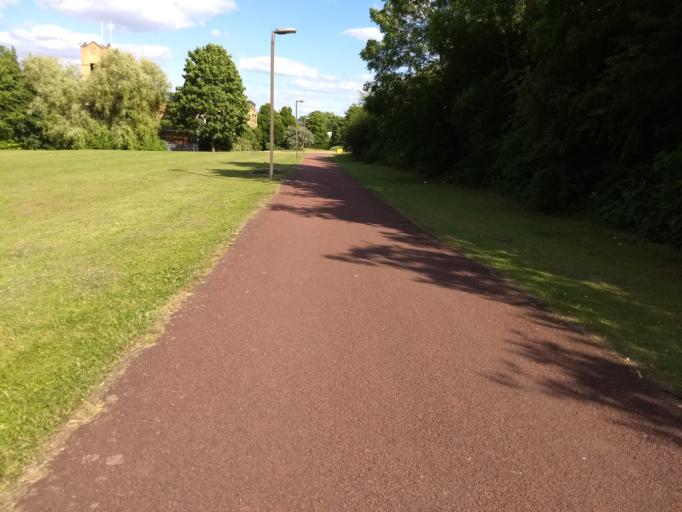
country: GB
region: England
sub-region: Milton Keynes
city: Shenley Church End
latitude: 52.0313
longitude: -0.7962
